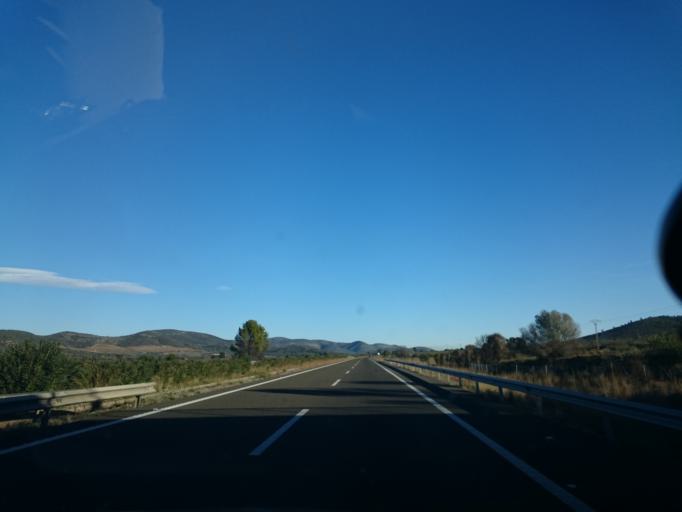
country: ES
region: Valencia
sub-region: Provincia de Castello
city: Alcala de Xivert
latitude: 40.3216
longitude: 0.2528
